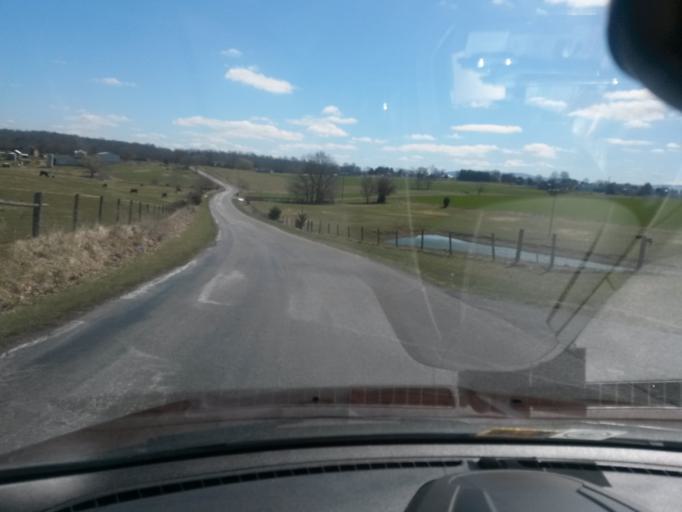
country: US
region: Virginia
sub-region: Augusta County
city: Stuarts Draft
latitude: 38.0444
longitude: -79.0434
